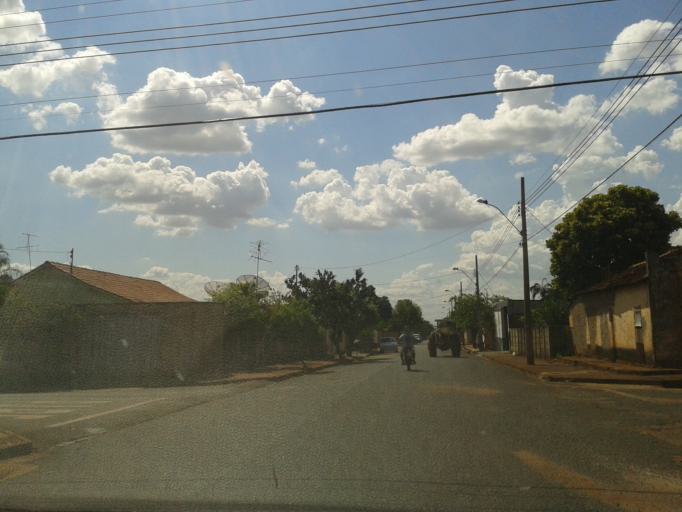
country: BR
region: Minas Gerais
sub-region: Centralina
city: Centralina
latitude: -18.7186
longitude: -49.2025
